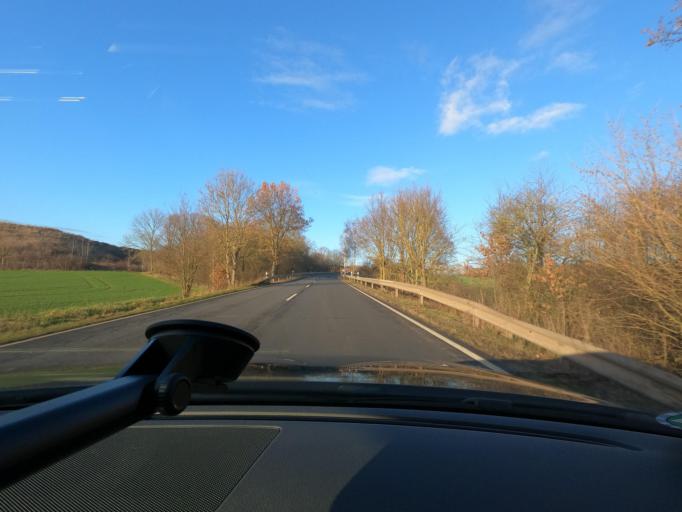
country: DE
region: Lower Saxony
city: Duderstadt
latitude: 51.5287
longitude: 10.2772
